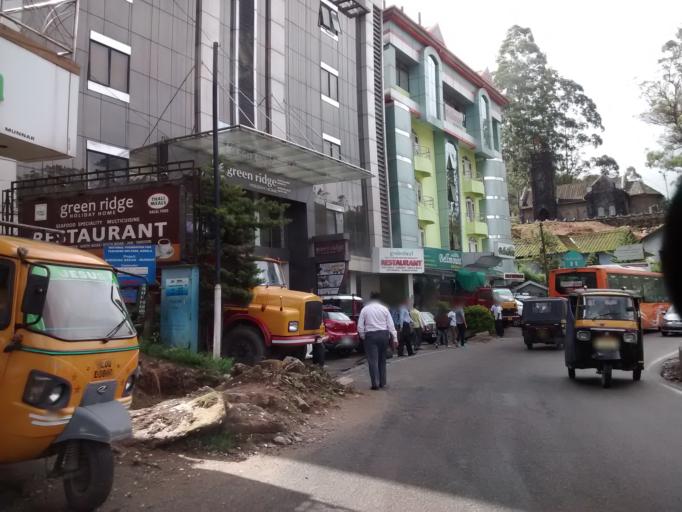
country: IN
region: Kerala
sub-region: Idukki
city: Munnar
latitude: 10.0798
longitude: 77.0619
